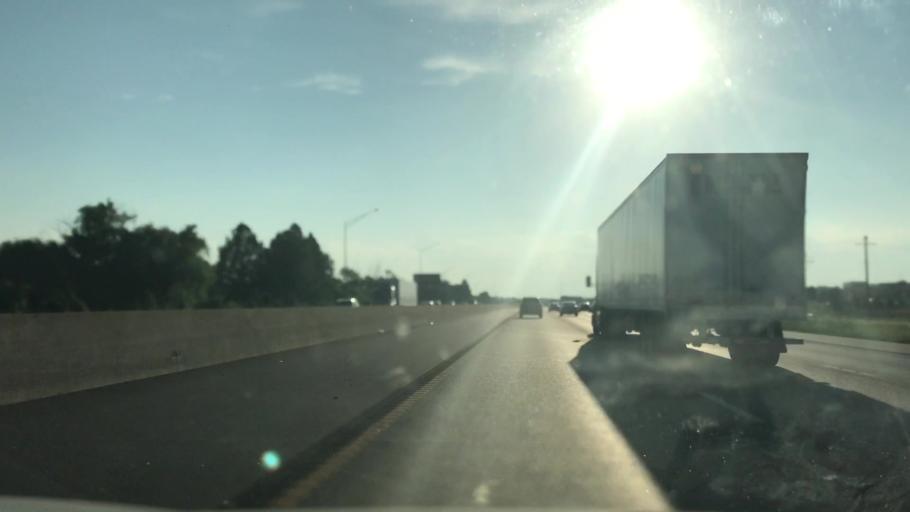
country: US
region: Missouri
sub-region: Saint Louis County
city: Chesterfield
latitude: 38.6694
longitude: -90.5837
